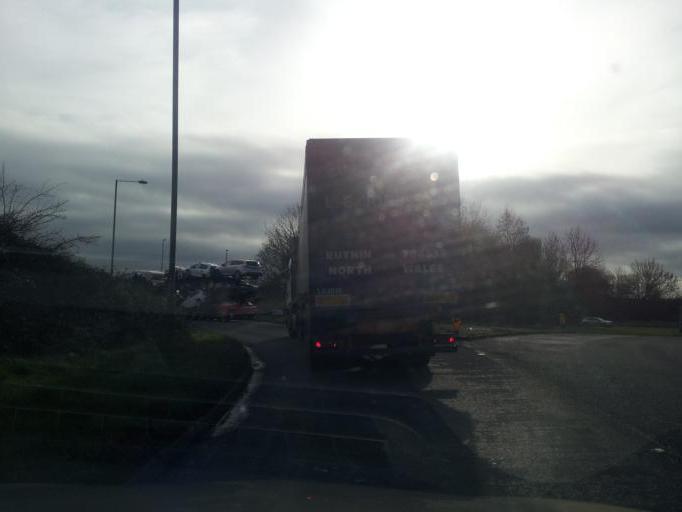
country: GB
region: England
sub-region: District of Rutland
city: Ketton
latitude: 52.6003
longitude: -0.5358
